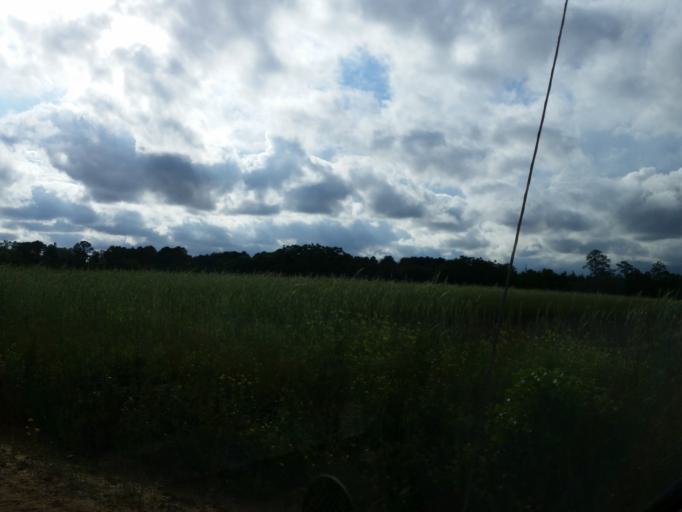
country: US
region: Georgia
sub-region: Dooly County
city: Vienna
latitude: 32.1389
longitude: -83.7899
